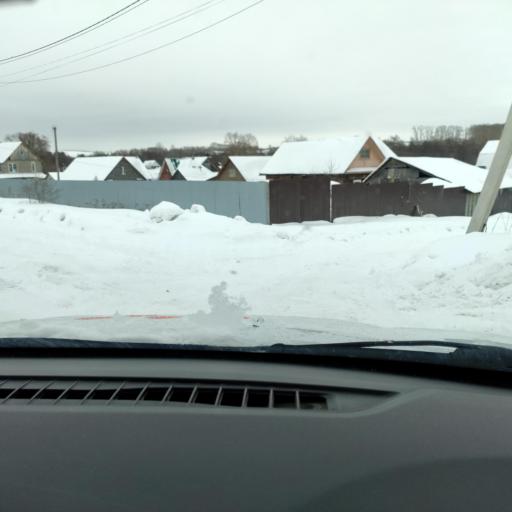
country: RU
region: Bashkortostan
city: Blagoveshchensk
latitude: 55.0488
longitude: 55.9786
